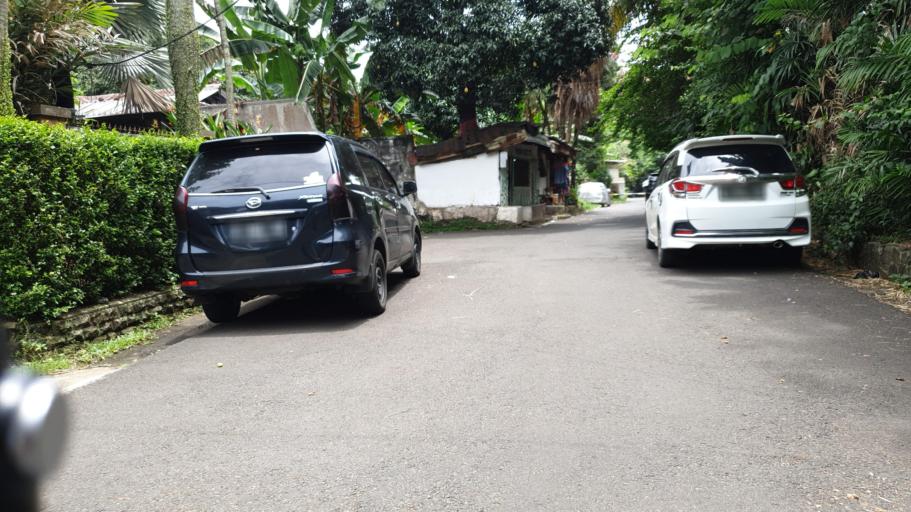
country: ID
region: West Java
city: Pamulang
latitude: -6.2972
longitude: 106.7813
